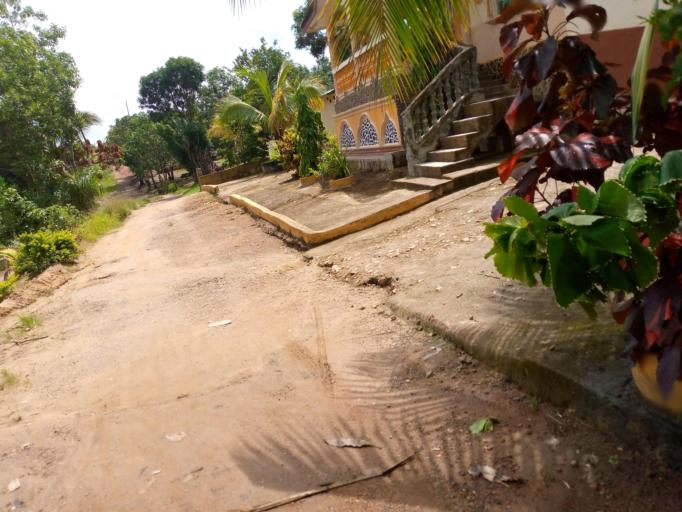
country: SL
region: Eastern Province
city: Kenema
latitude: 7.8795
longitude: -11.1635
